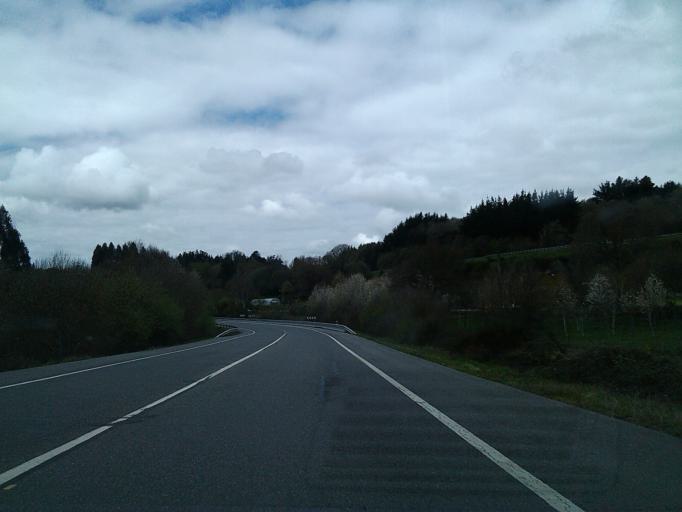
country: ES
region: Galicia
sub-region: Provincia de Lugo
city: Guitiriz
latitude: 43.1774
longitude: -7.8064
